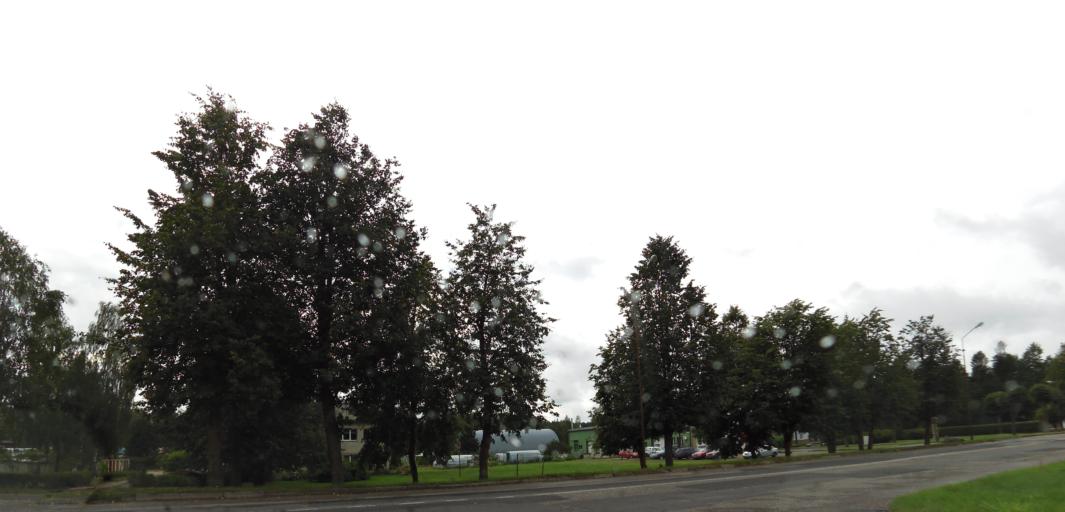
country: LT
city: Moletai
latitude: 55.2250
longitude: 25.4021
